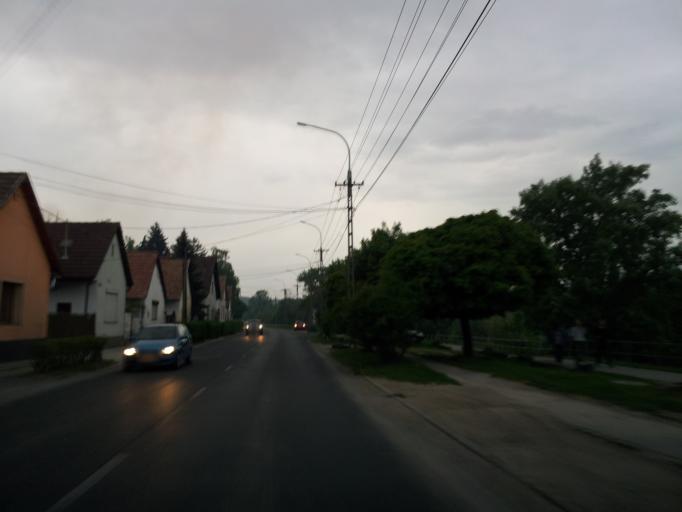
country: HU
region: Pest
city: Dunabogdany
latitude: 47.7977
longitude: 19.0260
